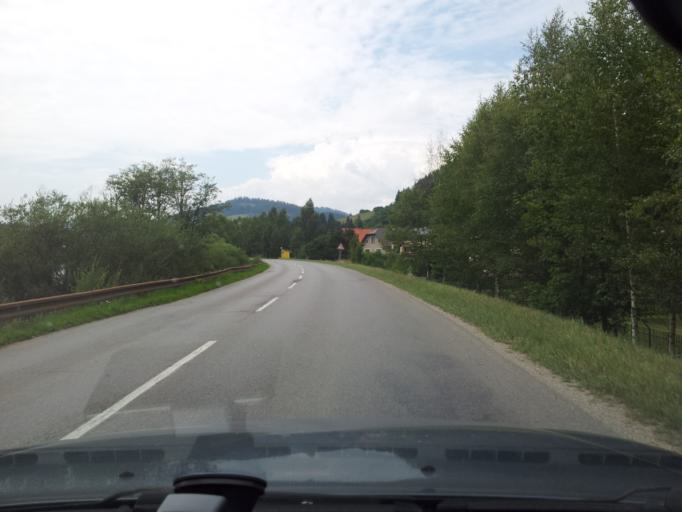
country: SK
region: Zilinsky
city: Namestovo
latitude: 49.3848
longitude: 19.3754
